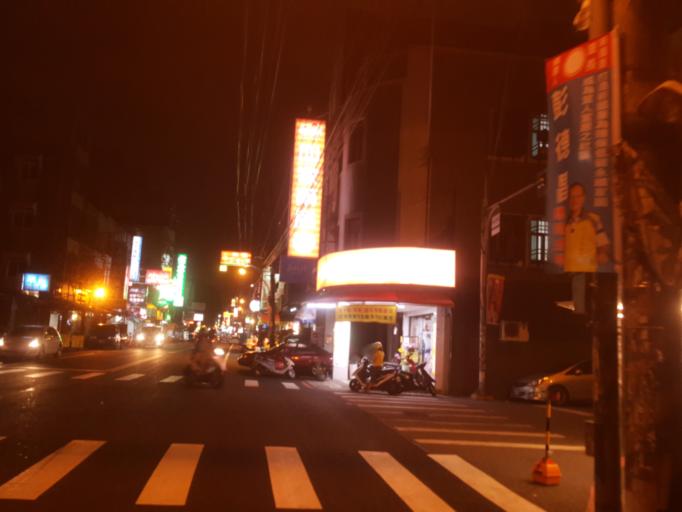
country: TW
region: Taiwan
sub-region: Hsinchu
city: Zhubei
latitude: 24.8419
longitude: 120.9987
